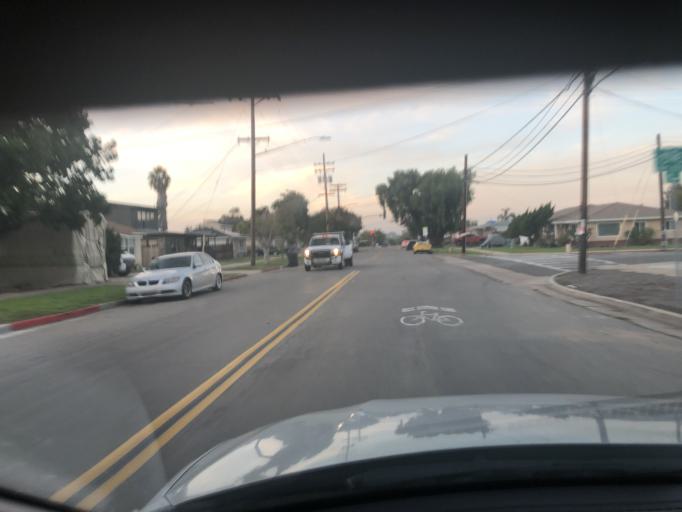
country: US
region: California
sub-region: San Diego County
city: Chula Vista
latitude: 32.6457
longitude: -117.0725
